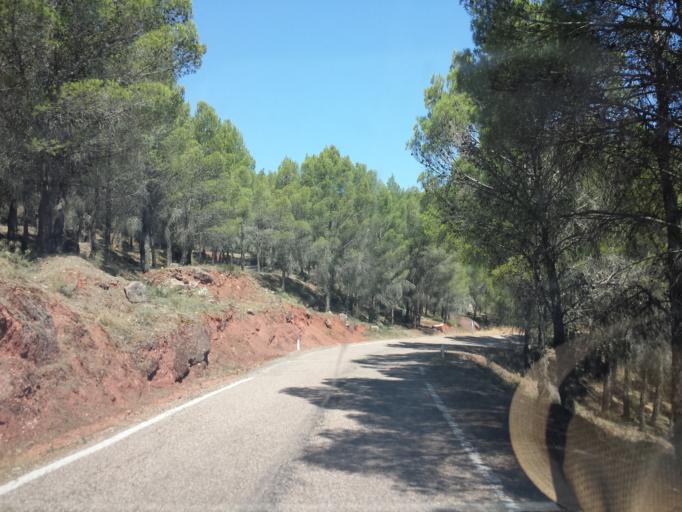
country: ES
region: Aragon
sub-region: Provincia de Zaragoza
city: Carenas
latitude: 41.2571
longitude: -1.8097
